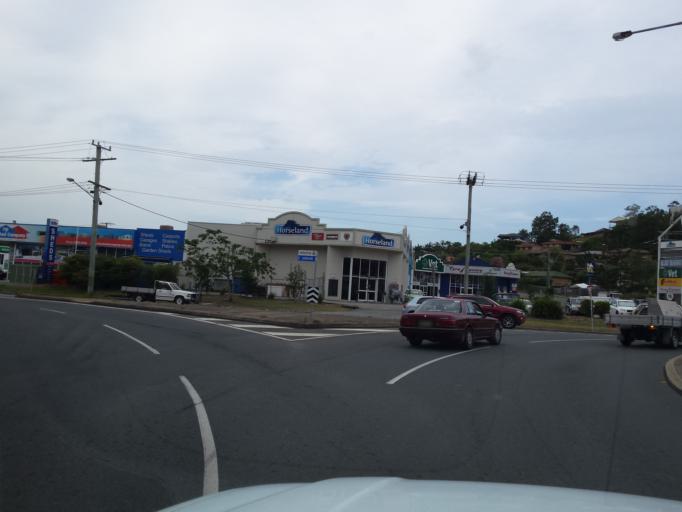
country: AU
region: Queensland
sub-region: Gold Coast
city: Nerang
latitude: -28.0066
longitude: 153.3431
